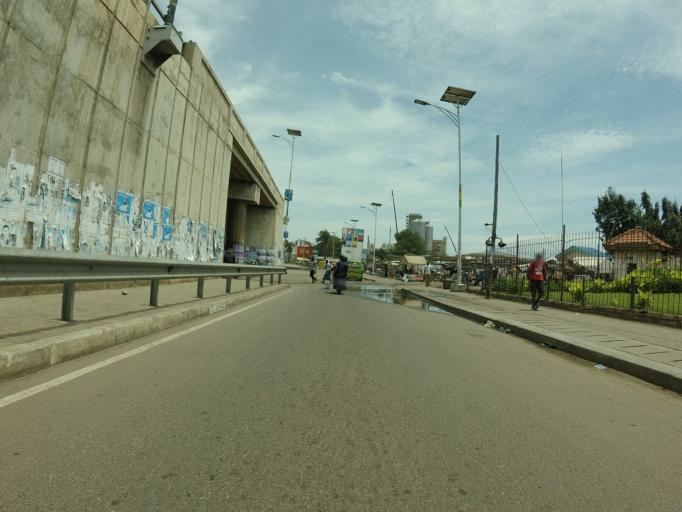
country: GH
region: Greater Accra
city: Accra
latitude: 5.5558
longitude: -0.2203
